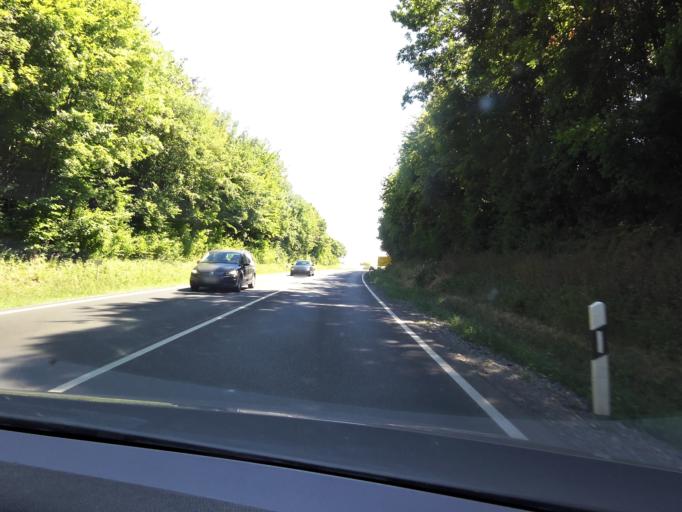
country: DE
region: Bavaria
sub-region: Regierungsbezirk Unterfranken
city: Reichenberg
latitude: 49.7357
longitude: 9.9341
